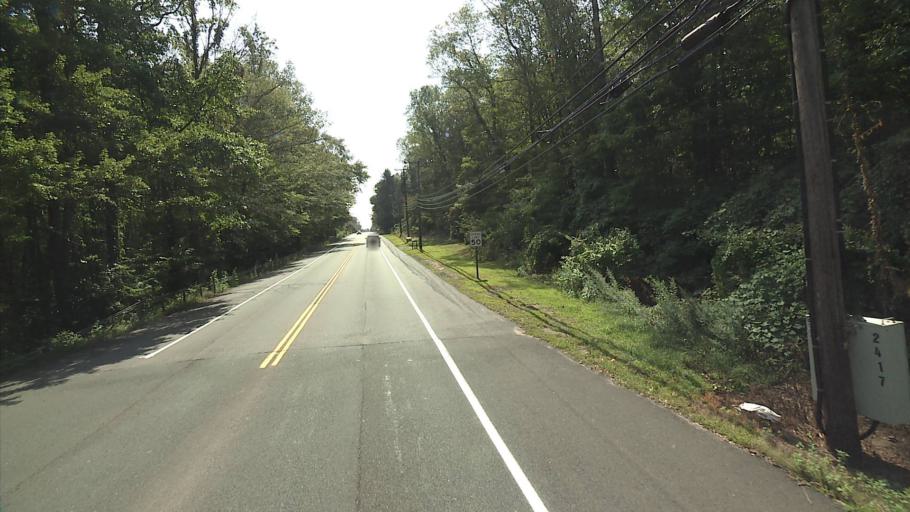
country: US
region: Connecticut
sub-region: New Haven County
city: Guilford
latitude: 41.3567
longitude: -72.6371
